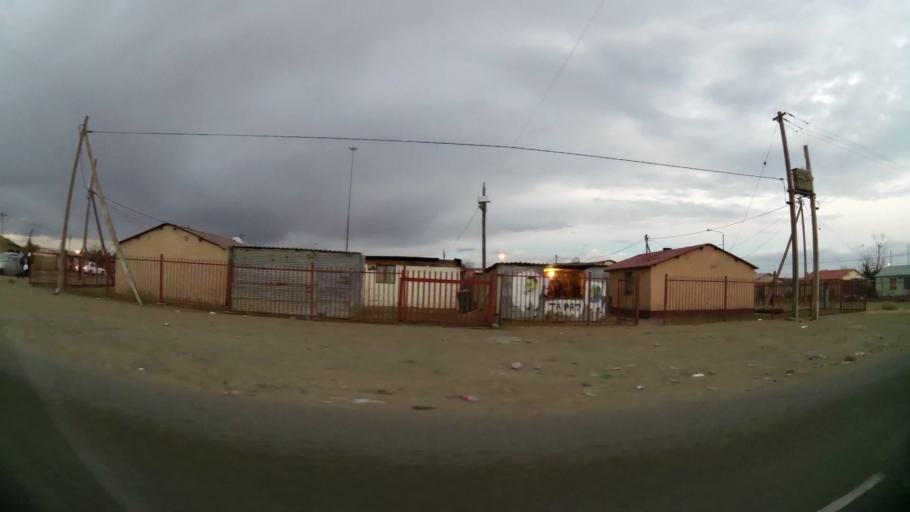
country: ZA
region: Orange Free State
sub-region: Lejweleputswa District Municipality
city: Welkom
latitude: -27.9654
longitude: 26.7857
